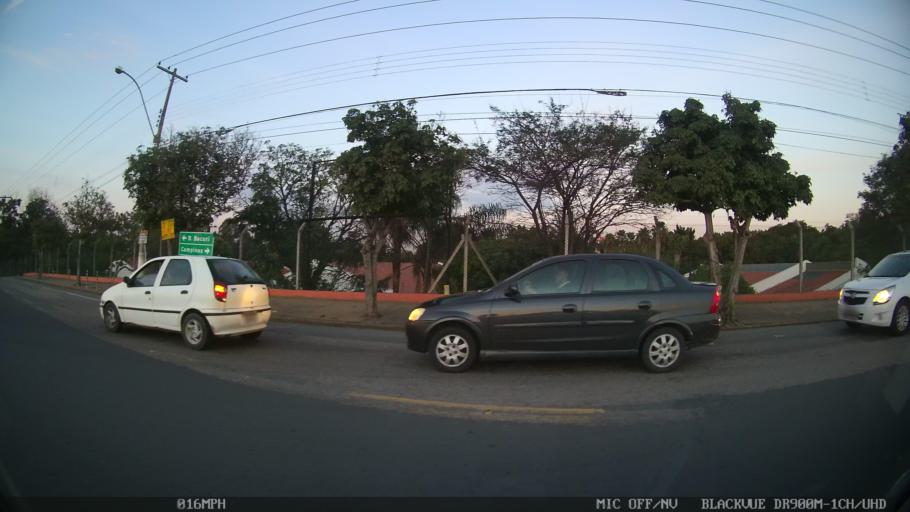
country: BR
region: Sao Paulo
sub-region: Campinas
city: Campinas
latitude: -22.9735
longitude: -47.1023
